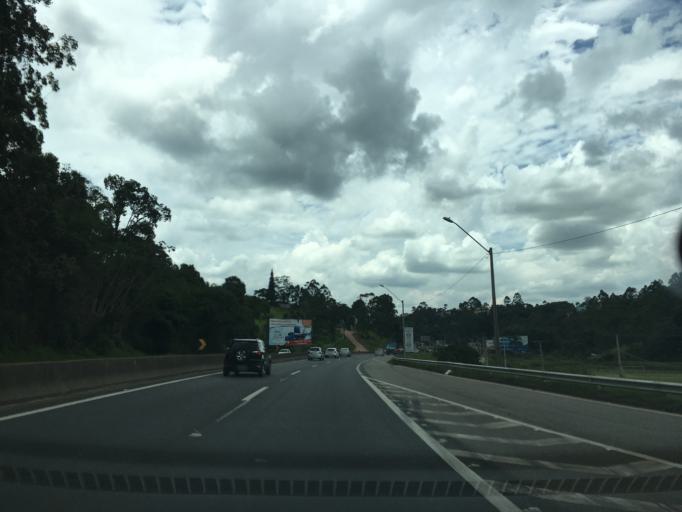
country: BR
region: Sao Paulo
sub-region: Mairipora
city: Mairipora
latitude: -23.2427
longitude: -46.5974
